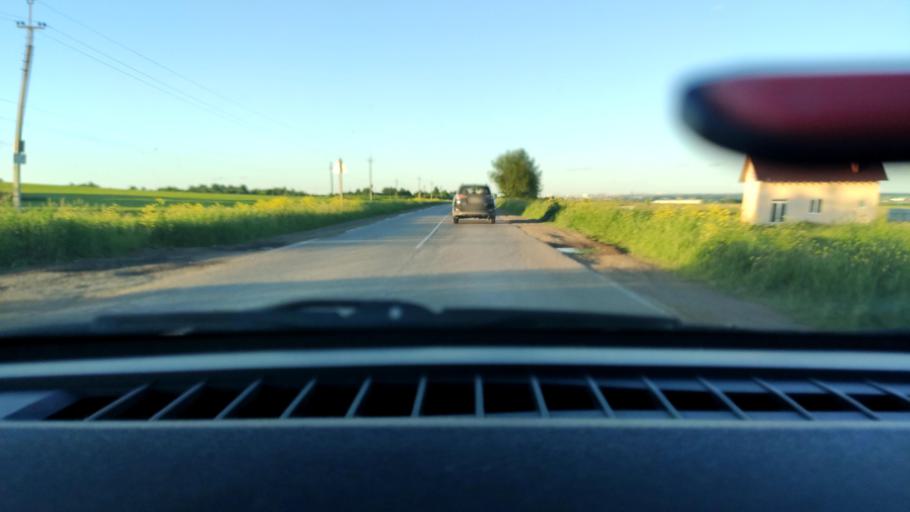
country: RU
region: Perm
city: Kultayevo
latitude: 57.9215
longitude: 55.9580
